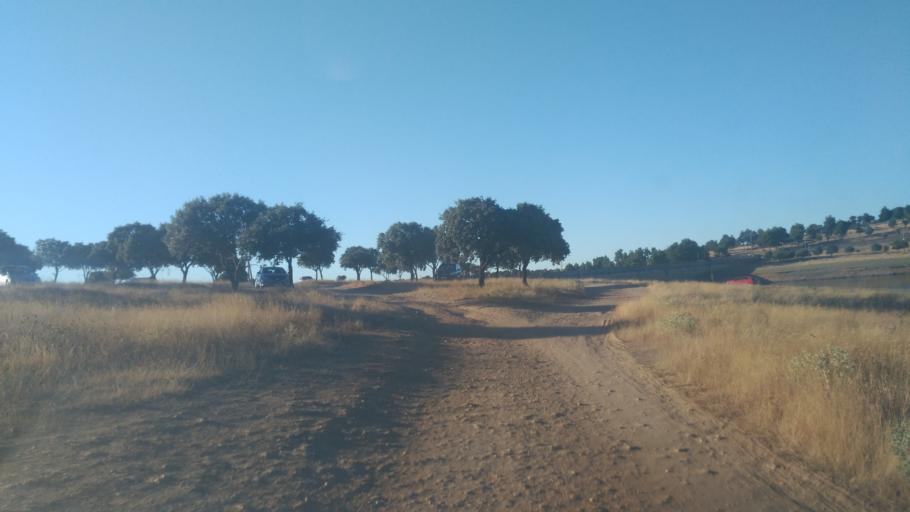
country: ES
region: Castille and Leon
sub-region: Provincia de Salamanca
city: Montejo
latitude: 40.6644
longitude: -5.6097
